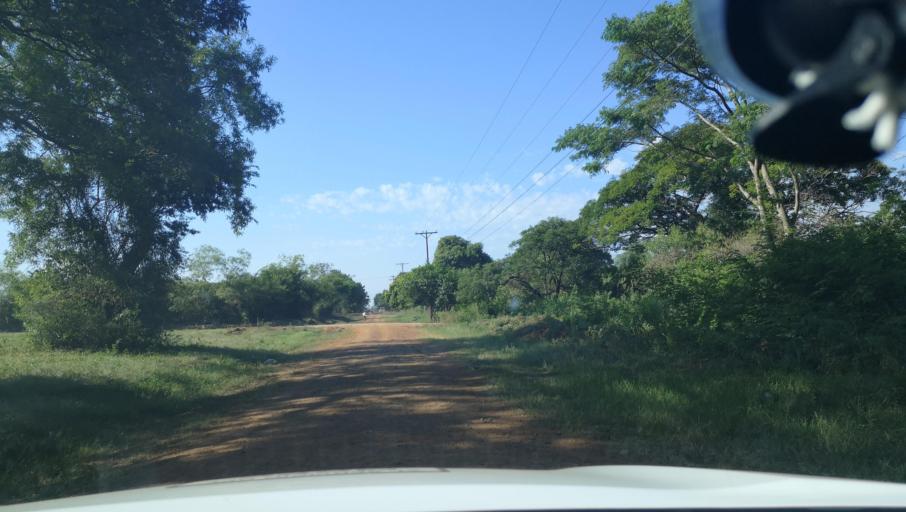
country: PY
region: Itapua
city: Carmen del Parana
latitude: -27.1681
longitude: -56.2383
